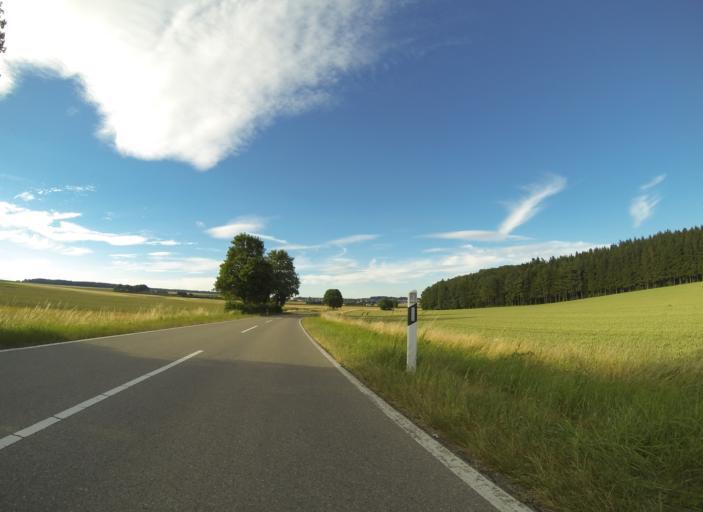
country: DE
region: Baden-Wuerttemberg
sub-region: Tuebingen Region
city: Altheim
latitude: 48.3261
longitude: 9.8033
